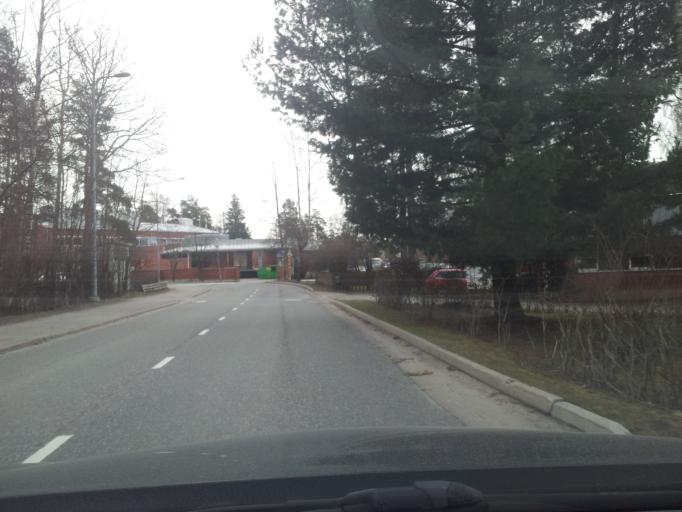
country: FI
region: Uusimaa
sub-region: Helsinki
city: Kilo
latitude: 60.2046
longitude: 24.8029
